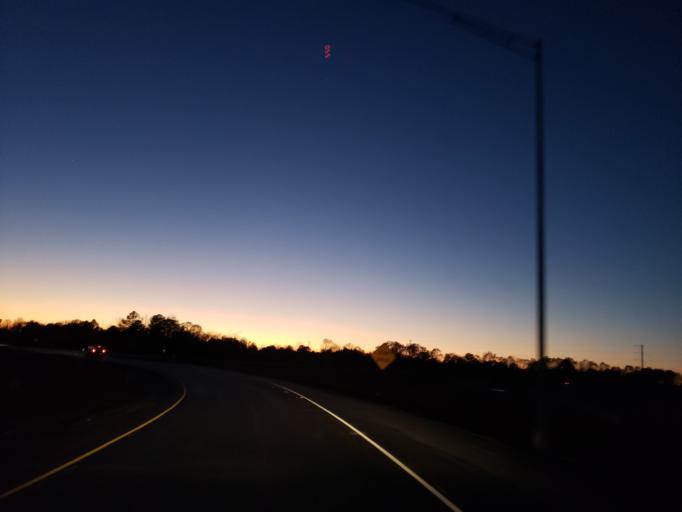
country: US
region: Mississippi
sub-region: Forrest County
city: Glendale
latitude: 31.3847
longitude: -89.3255
